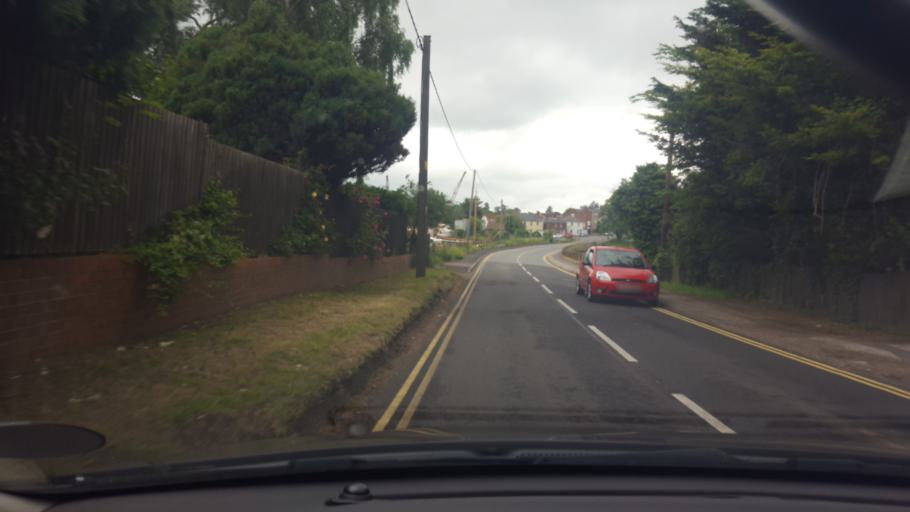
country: GB
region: England
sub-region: Essex
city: Saint Osyth
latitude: 51.7958
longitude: 1.0654
